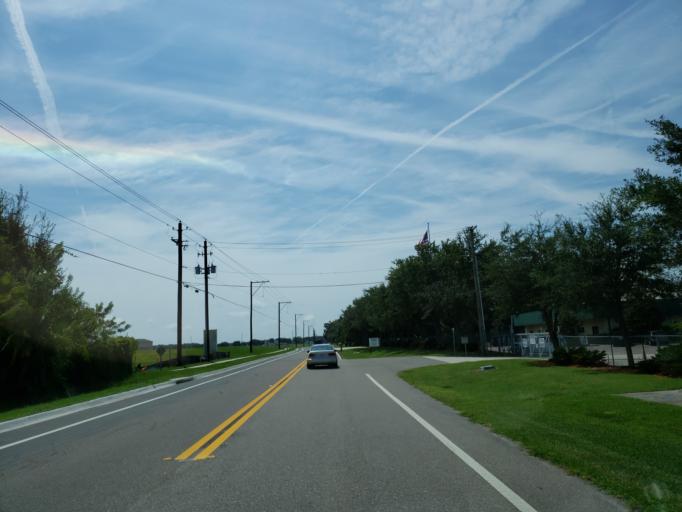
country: US
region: Florida
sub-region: Hillsborough County
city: Riverview
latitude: 27.8428
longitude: -82.3433
